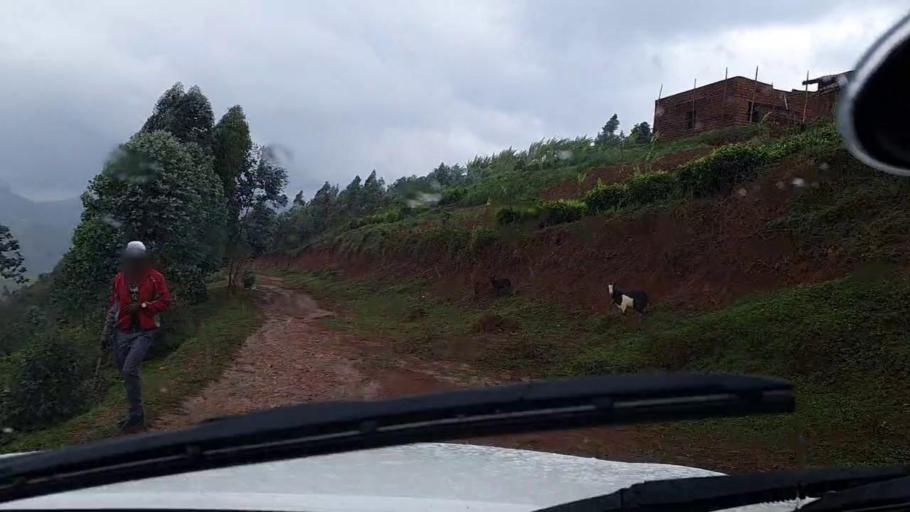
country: RW
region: Western Province
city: Kibuye
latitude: -2.1109
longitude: 29.4809
